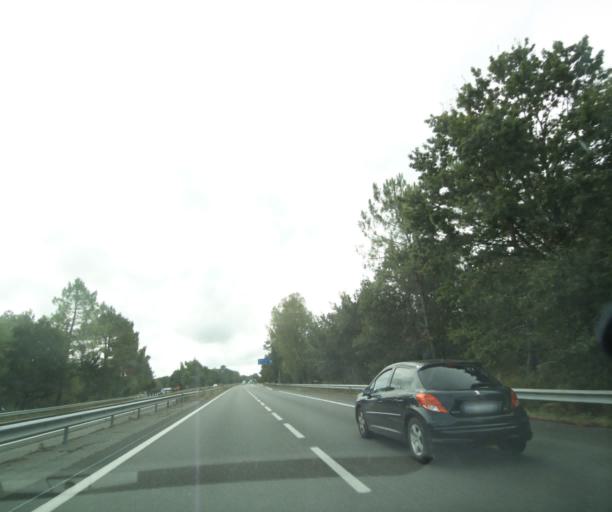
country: FR
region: Poitou-Charentes
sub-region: Departement de la Charente-Maritime
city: Saint-Genis-de-Saintonge
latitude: 45.4452
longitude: -0.6096
